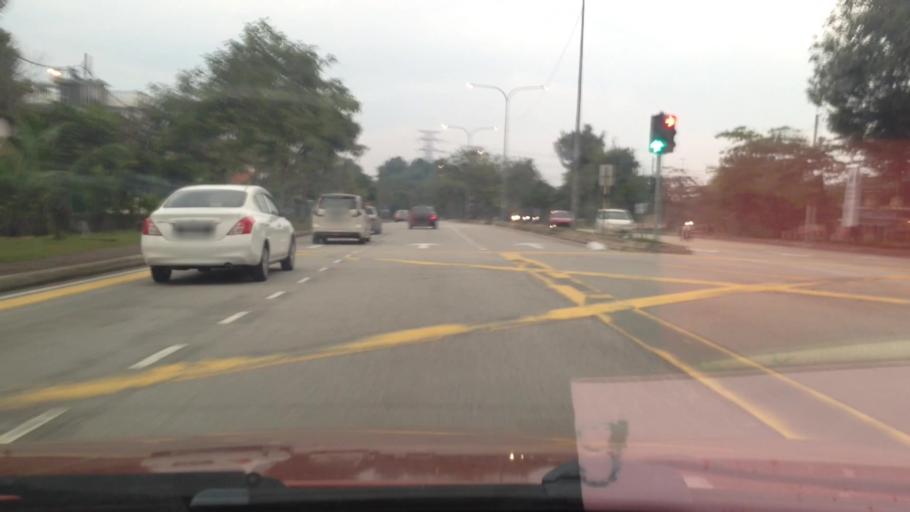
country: MY
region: Selangor
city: Subang Jaya
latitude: 3.0573
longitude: 101.5716
